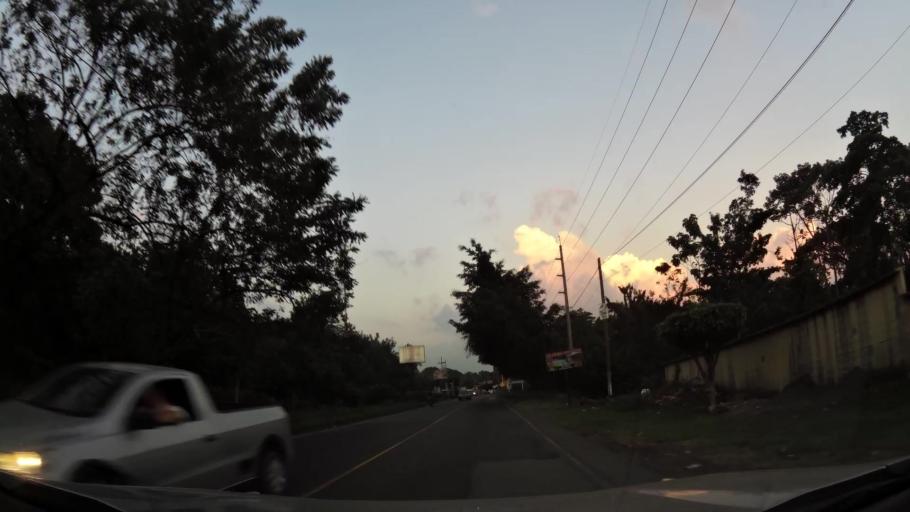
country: GT
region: Retalhuleu
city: Santa Cruz Mulua
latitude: 14.5845
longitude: -91.6241
